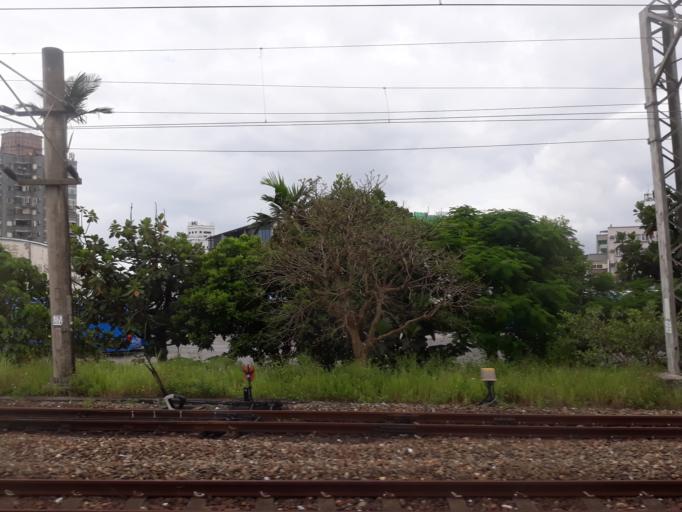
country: TW
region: Taiwan
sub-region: Yilan
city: Yilan
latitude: 24.7085
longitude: 121.7737
